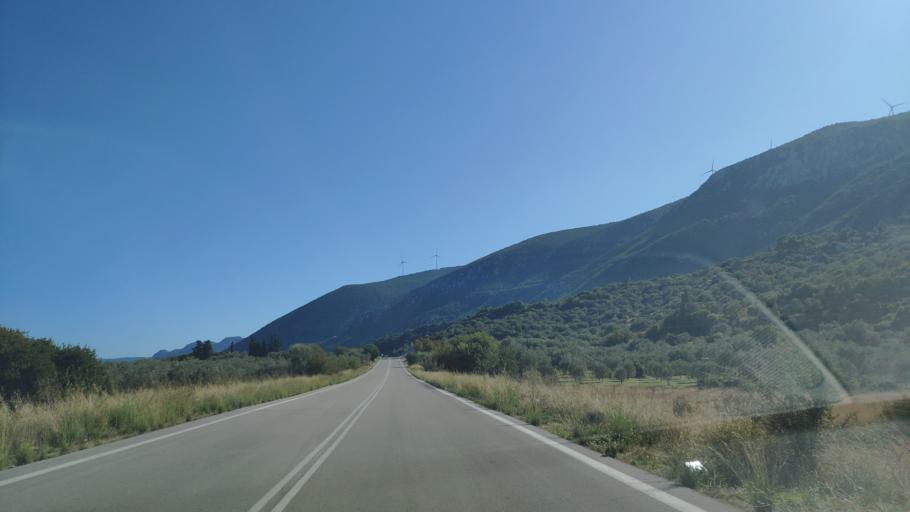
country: GR
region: Peloponnese
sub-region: Nomos Argolidos
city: Palaia Epidavros
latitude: 37.5692
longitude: 23.2508
